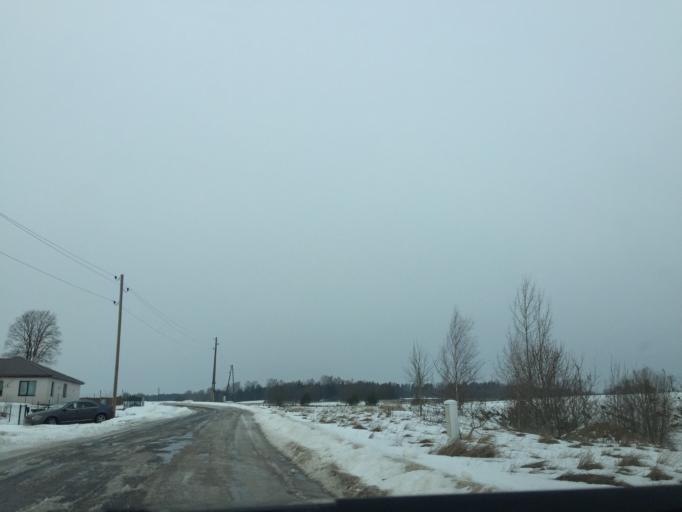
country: LV
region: Ikskile
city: Ikskile
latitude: 56.8446
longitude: 24.4606
